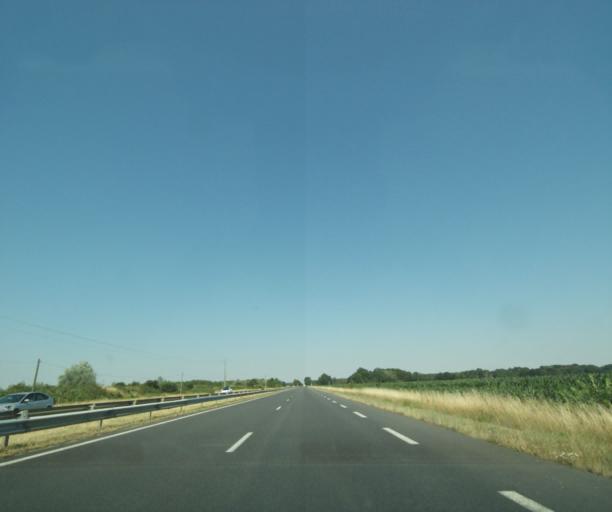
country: FR
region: Champagne-Ardenne
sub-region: Departement de la Haute-Marne
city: Villiers-en-Lieu
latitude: 48.6657
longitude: 4.7921
